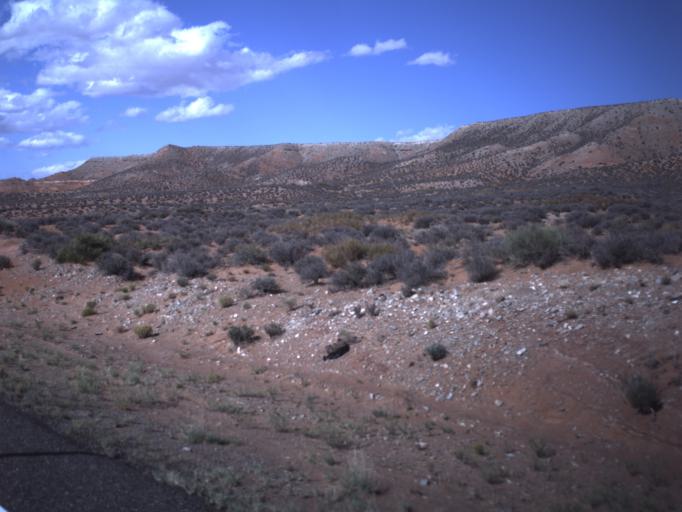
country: US
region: Utah
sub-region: Wayne County
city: Loa
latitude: 38.0788
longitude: -110.6113
